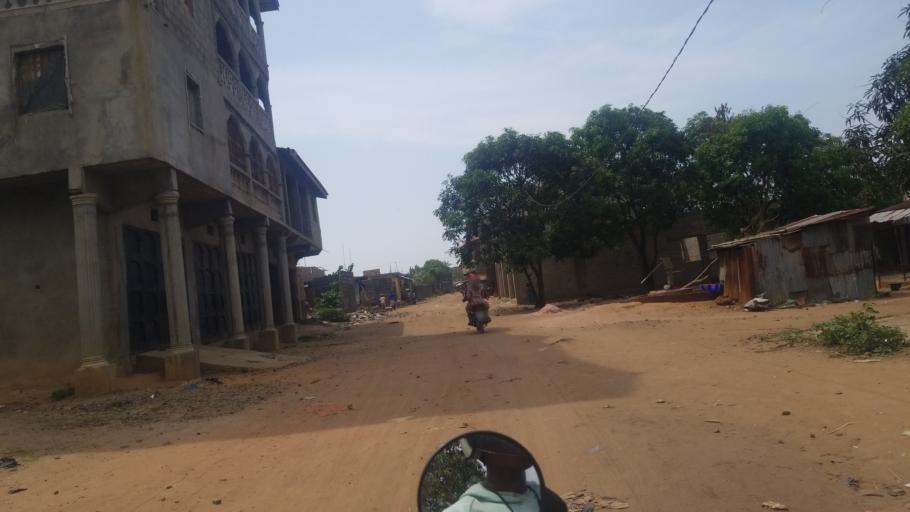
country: SL
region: Western Area
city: Waterloo
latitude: 8.3283
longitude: -13.0488
